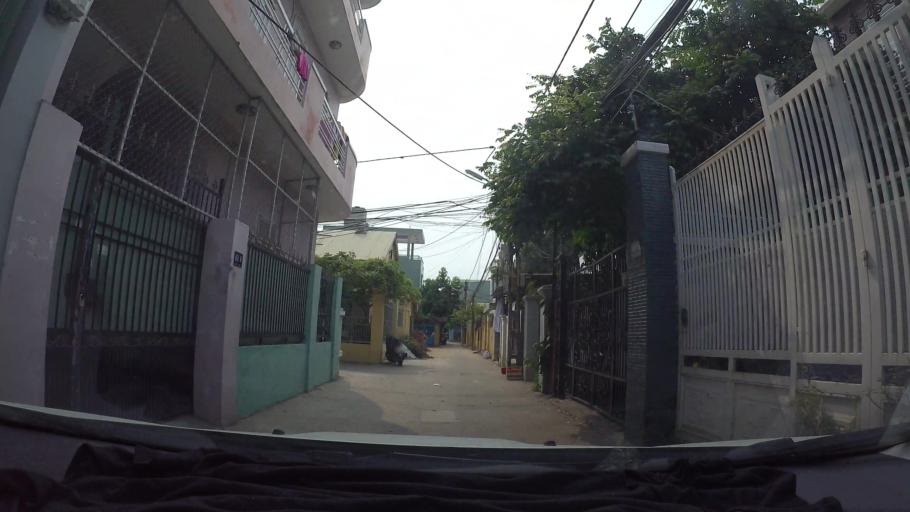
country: VN
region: Da Nang
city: Son Tra
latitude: 16.0424
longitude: 108.2197
